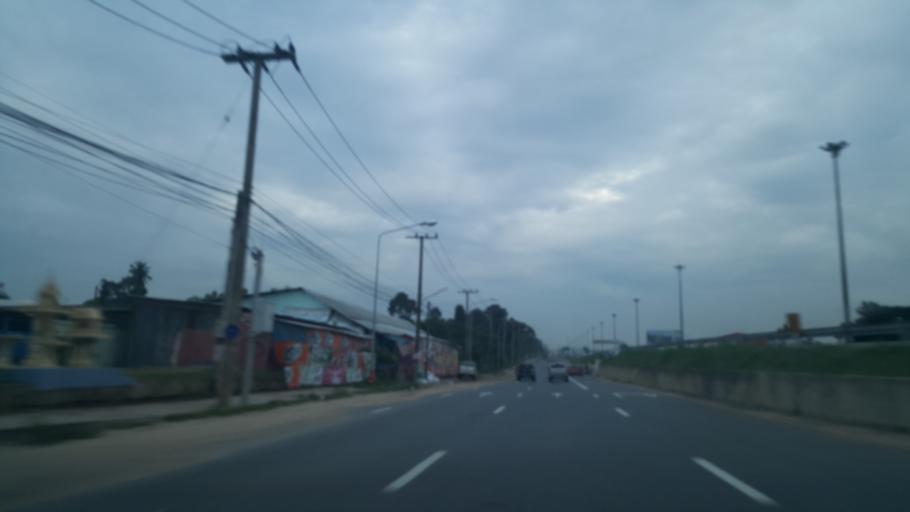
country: TH
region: Chon Buri
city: Ban Talat Bueng
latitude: 13.0025
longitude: 100.9936
